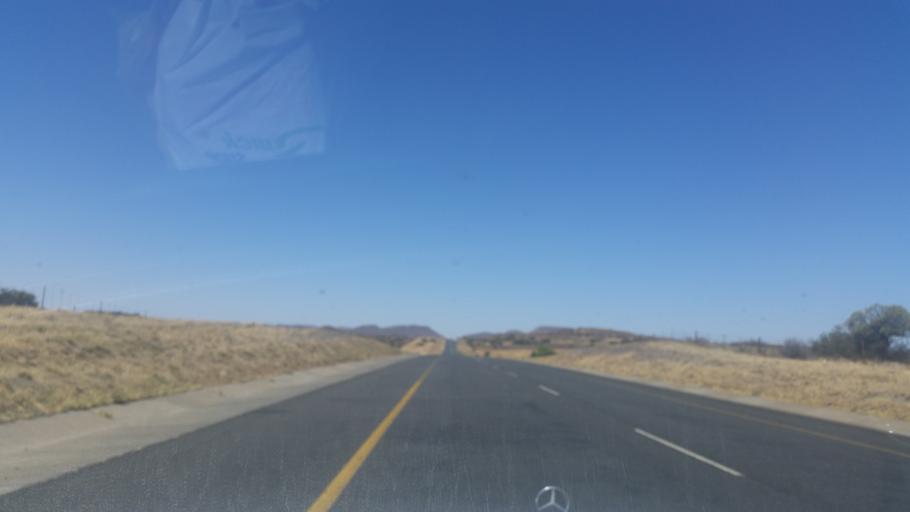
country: ZA
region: Northern Cape
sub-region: Pixley ka Seme District Municipality
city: Colesberg
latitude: -30.6180
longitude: 25.3142
